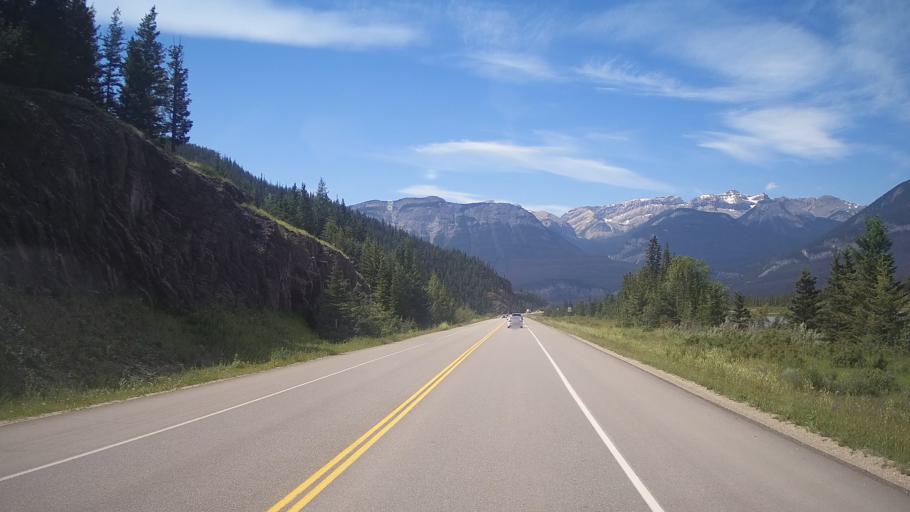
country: CA
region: Alberta
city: Jasper Park Lodge
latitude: 53.0519
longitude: -118.0724
